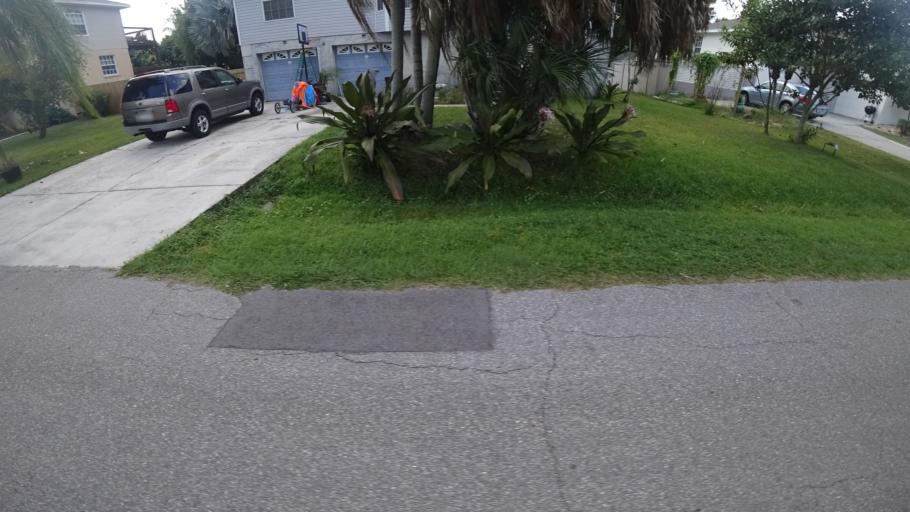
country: US
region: Florida
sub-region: Manatee County
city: Memphis
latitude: 27.5610
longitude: -82.5671
